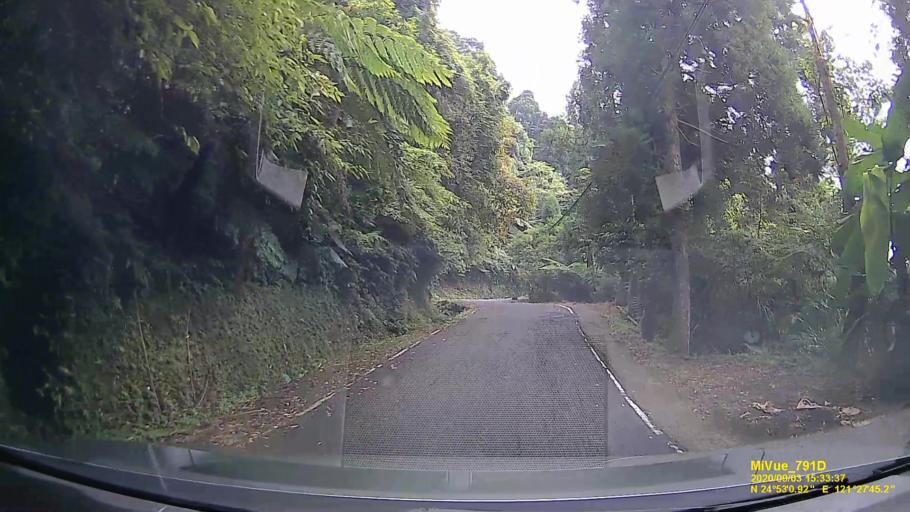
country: TW
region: Taipei
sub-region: Taipei
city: Banqiao
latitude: 24.8835
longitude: 121.4626
